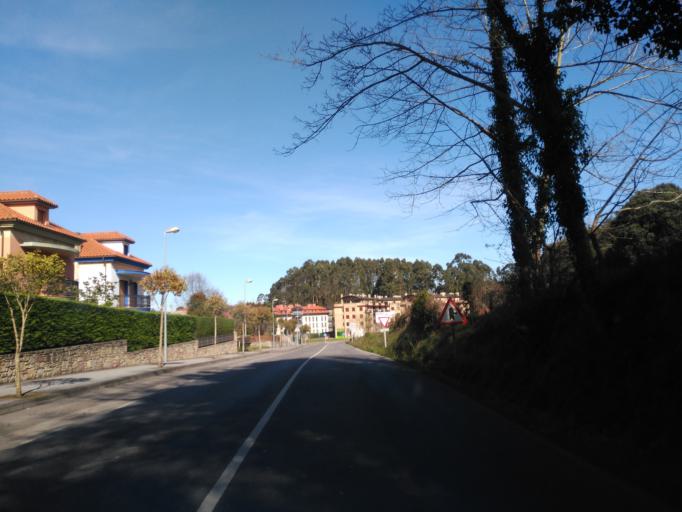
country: ES
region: Asturias
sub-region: Province of Asturias
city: Llanes
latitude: 43.4120
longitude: -4.7542
